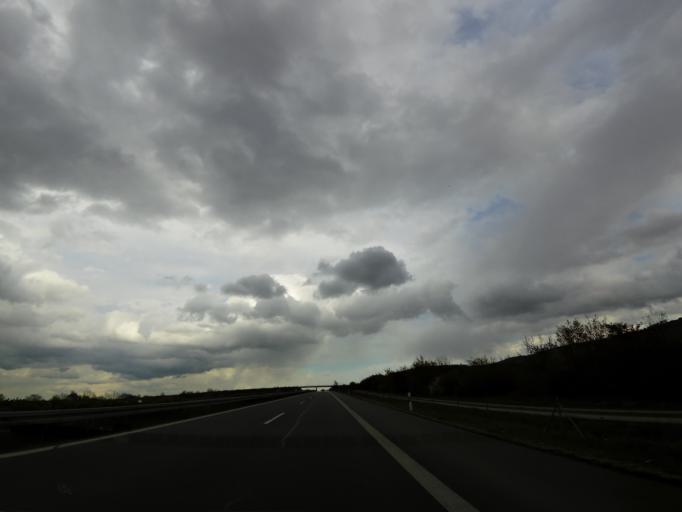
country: DE
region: Saxony-Anhalt
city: Wernigerode
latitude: 51.8458
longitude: 10.8344
